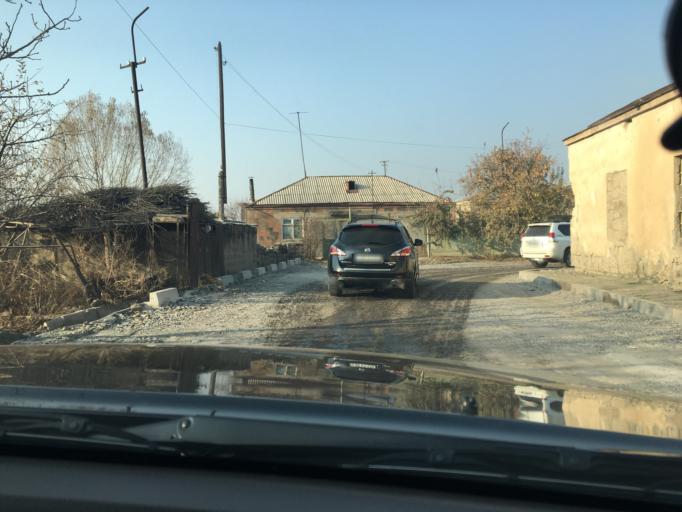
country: AM
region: Armavir
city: Janfida
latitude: 40.0427
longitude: 44.0254
